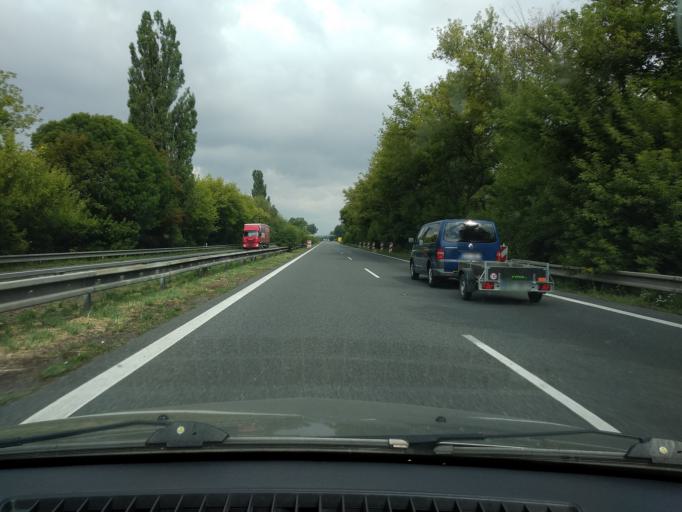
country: CZ
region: Olomoucky
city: Skrben
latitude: 49.6243
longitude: 17.1715
